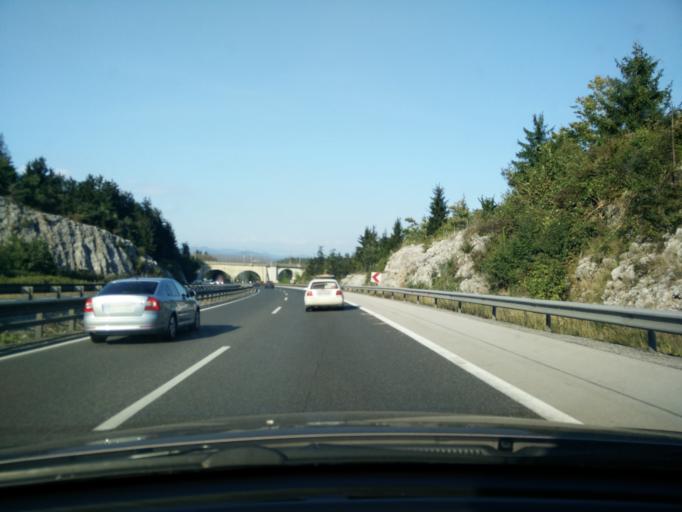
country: SI
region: Vrhnika
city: Vrhnika
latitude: 45.9382
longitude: 14.2755
